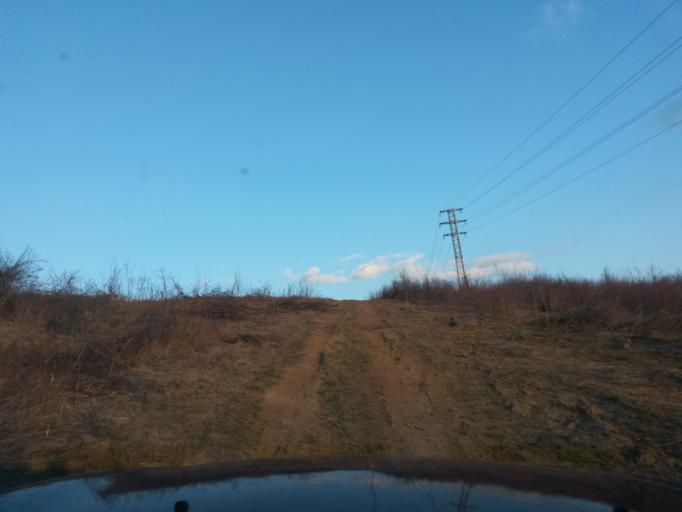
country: SK
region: Kosicky
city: Kosice
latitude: 48.6961
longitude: 21.3476
